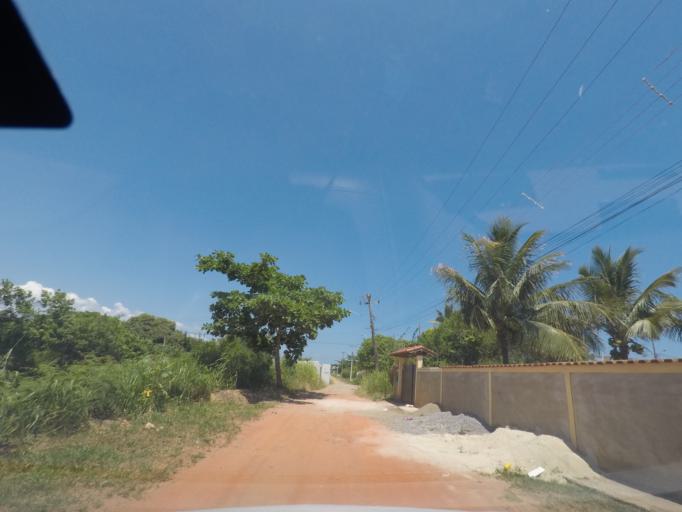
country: BR
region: Rio de Janeiro
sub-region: Marica
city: Marica
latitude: -22.9715
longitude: -42.9329
